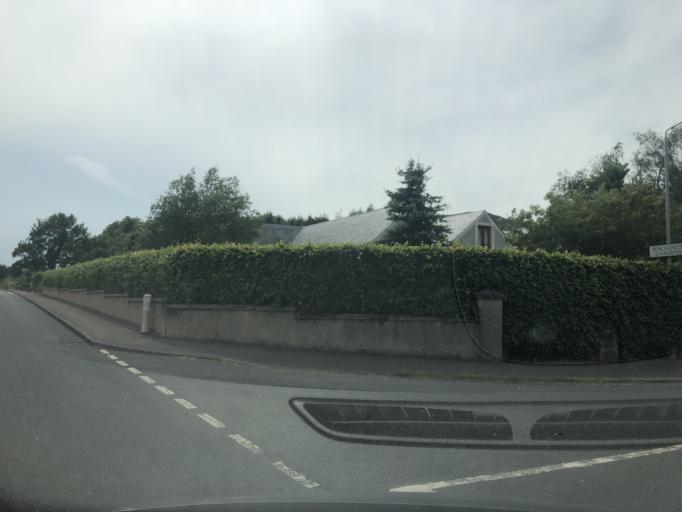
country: GB
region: Scotland
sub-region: The Scottish Borders
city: West Linton
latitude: 55.7037
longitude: -3.4281
